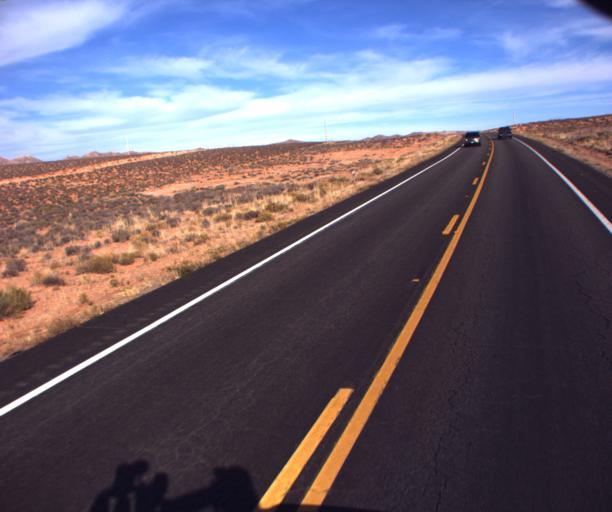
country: US
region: Arizona
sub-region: Apache County
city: Many Farms
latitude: 36.9253
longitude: -109.5910
